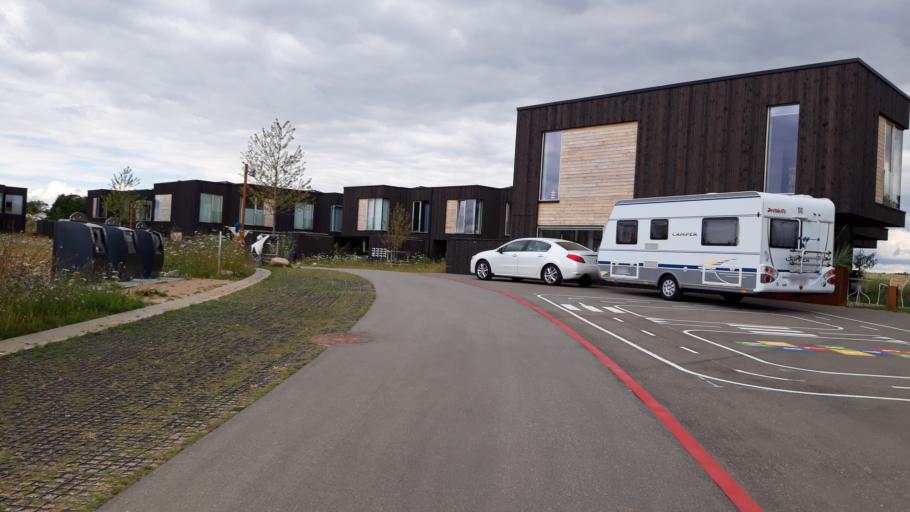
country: DK
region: Central Jutland
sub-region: Arhus Kommune
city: Lystrup
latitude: 56.2351
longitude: 10.2053
